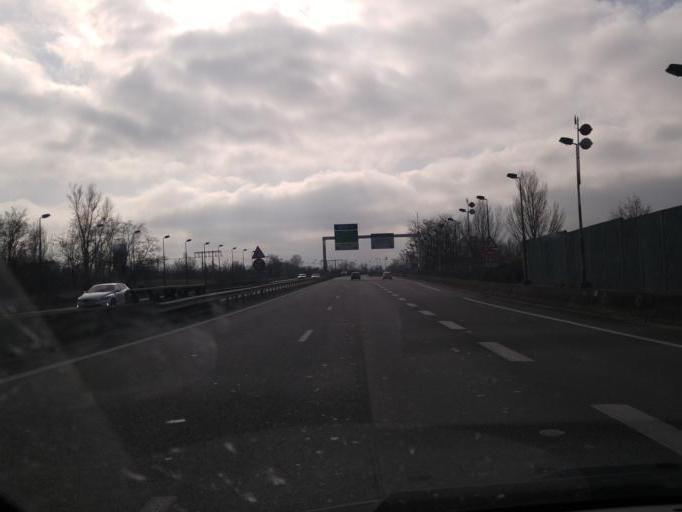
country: FR
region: Midi-Pyrenees
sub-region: Departement de la Haute-Garonne
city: Blagnac
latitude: 43.6129
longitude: 1.3867
